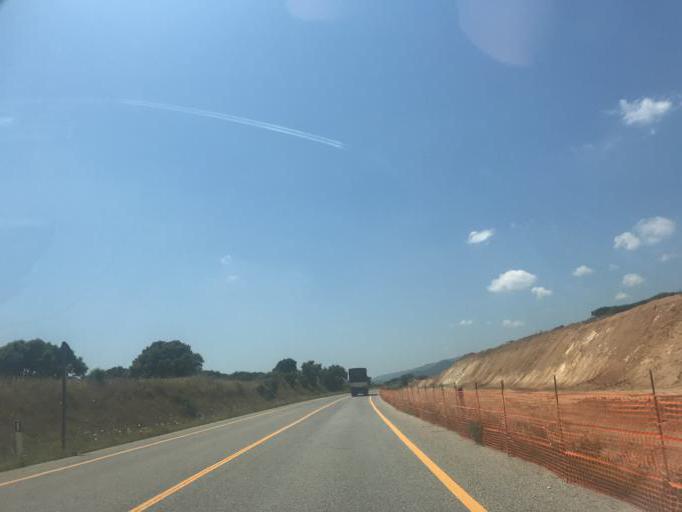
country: IT
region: Sardinia
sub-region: Provincia di Olbia-Tempio
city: Berchidda
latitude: 40.7788
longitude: 9.2357
